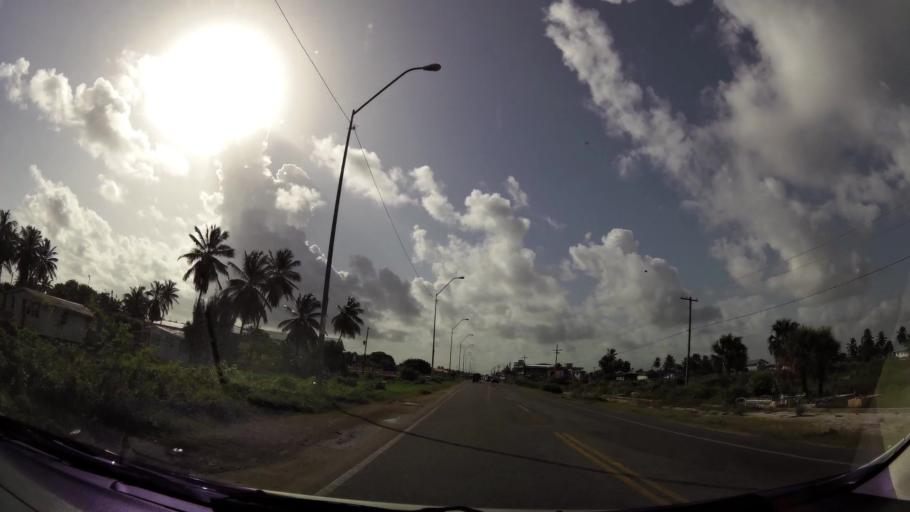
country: GY
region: Demerara-Mahaica
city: Georgetown
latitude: 6.8094
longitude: -58.0575
